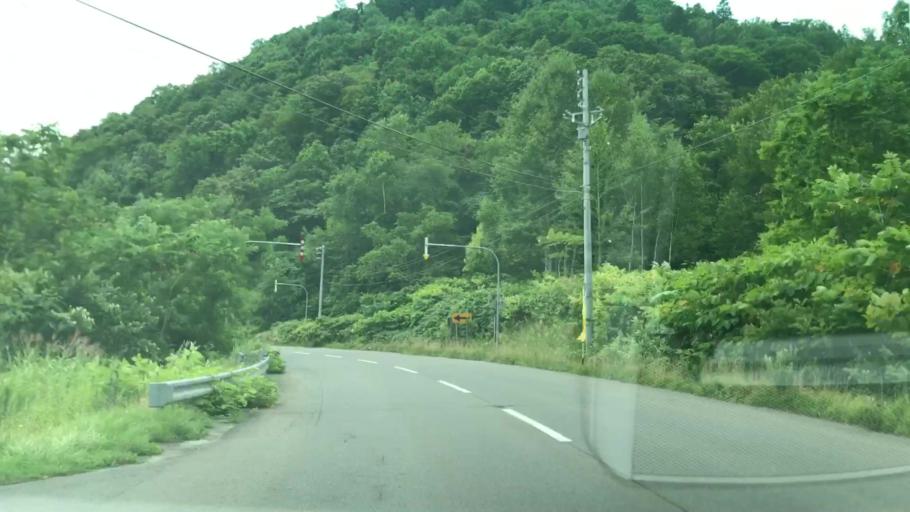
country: JP
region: Hokkaido
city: Yoichi
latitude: 43.0392
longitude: 140.8598
